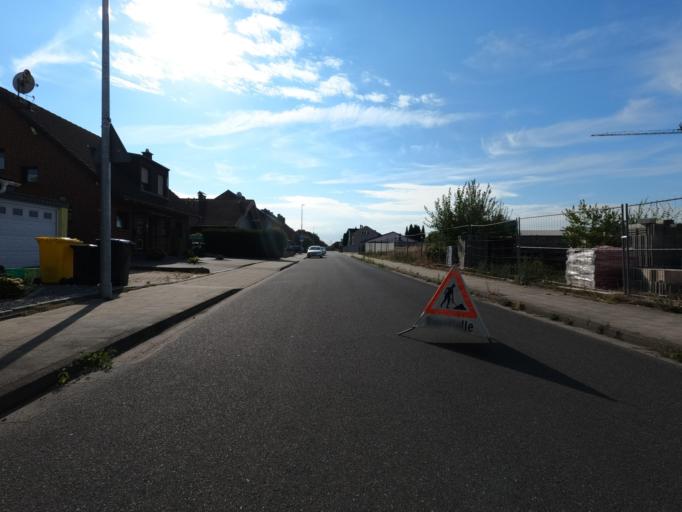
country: DE
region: North Rhine-Westphalia
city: Huckelhoven
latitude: 51.0988
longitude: 6.2108
